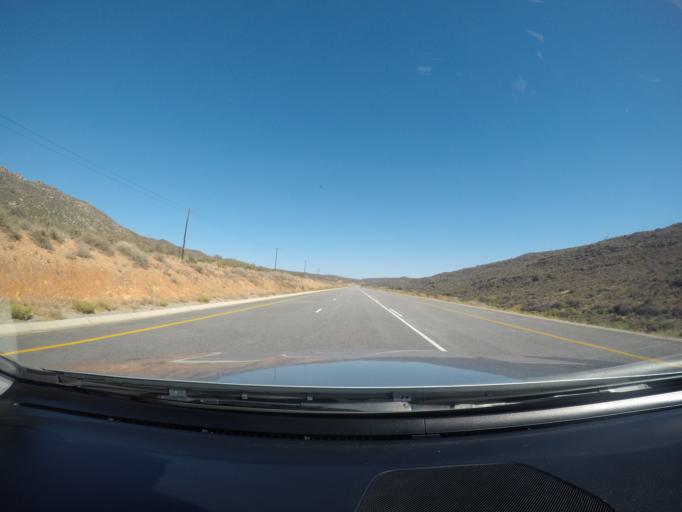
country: ZA
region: Western Cape
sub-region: West Coast District Municipality
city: Clanwilliam
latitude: -32.3452
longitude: 18.9277
